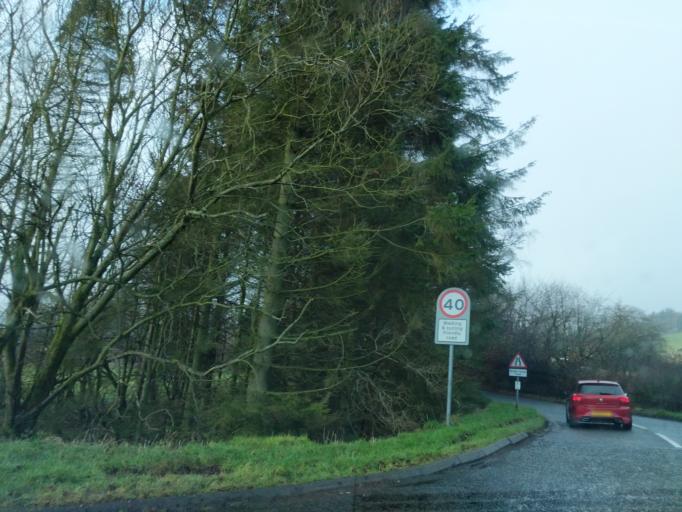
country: GB
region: Scotland
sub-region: Fife
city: Saline
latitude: 56.1895
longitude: -3.5415
